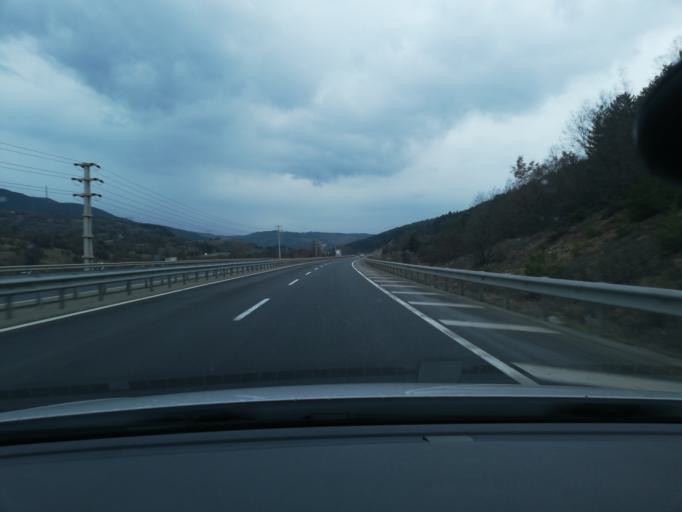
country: TR
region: Bolu
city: Gokcesu
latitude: 40.7427
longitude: 31.8471
